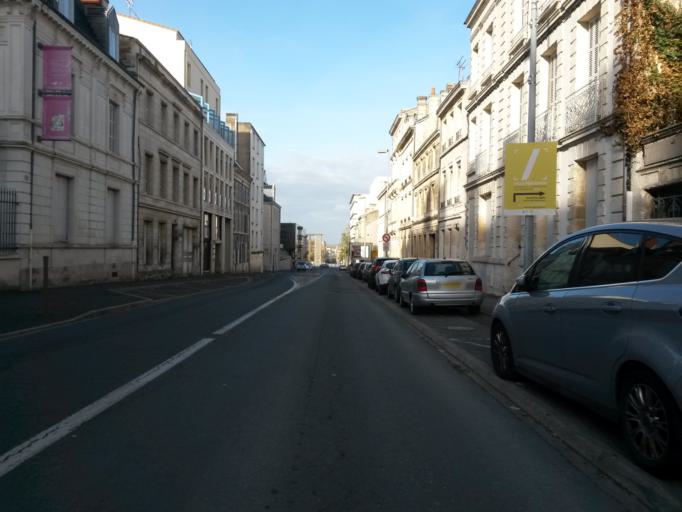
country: FR
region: Poitou-Charentes
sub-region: Departement des Deux-Sevres
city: Niort
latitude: 46.3213
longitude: -0.4545
